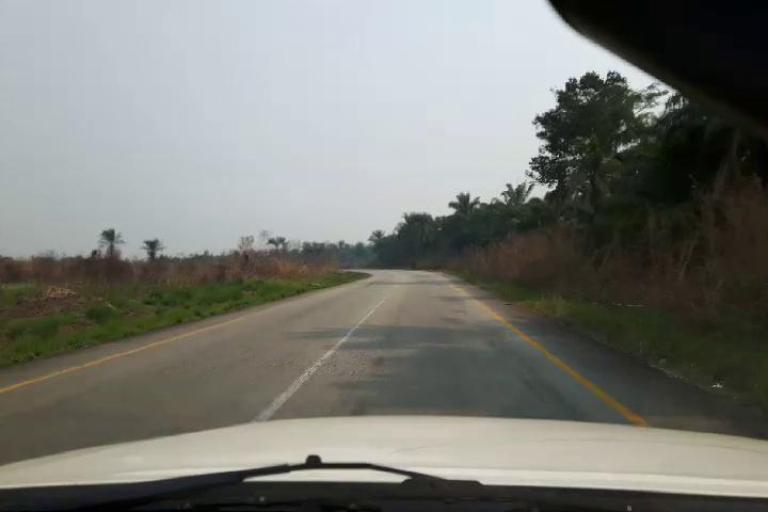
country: SL
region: Southern Province
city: Largo
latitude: 8.2152
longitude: -12.0738
